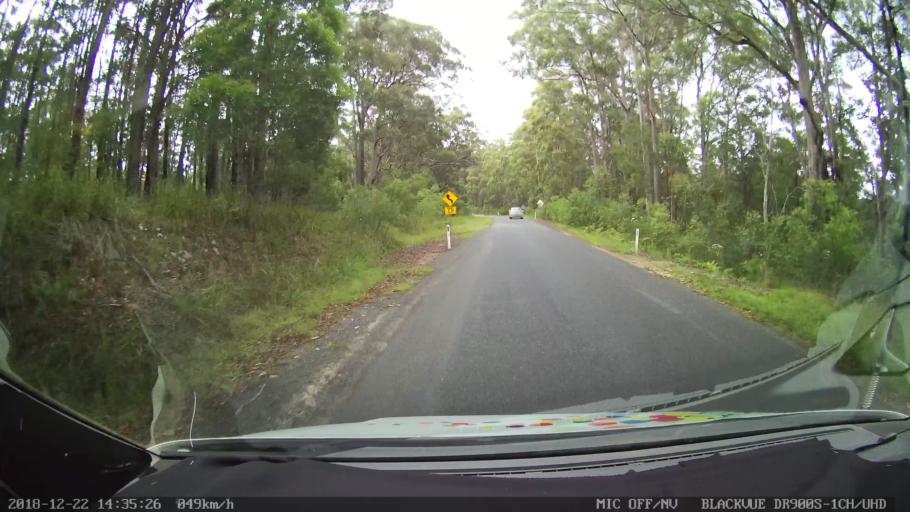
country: AU
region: New South Wales
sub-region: Bellingen
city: Dorrigo
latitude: -30.1238
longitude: 152.6145
